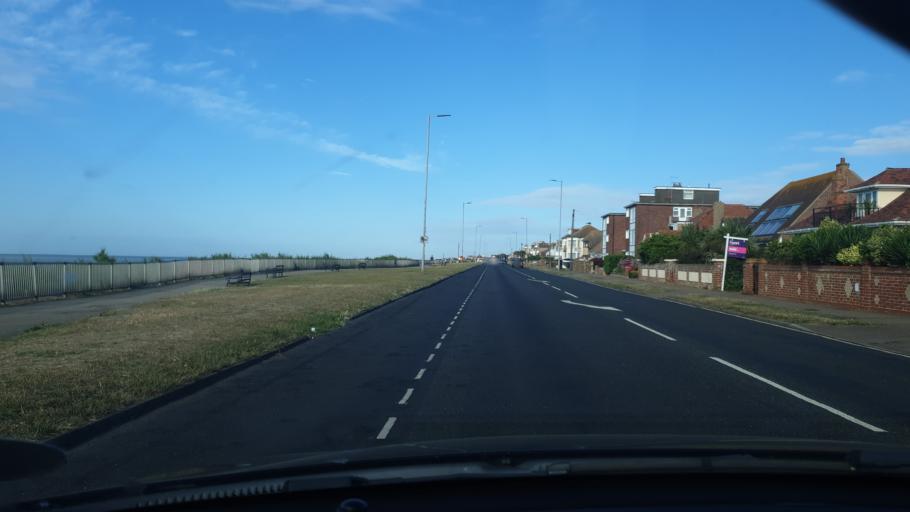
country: GB
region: England
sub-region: Essex
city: Clacton-on-Sea
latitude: 51.8000
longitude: 1.1908
